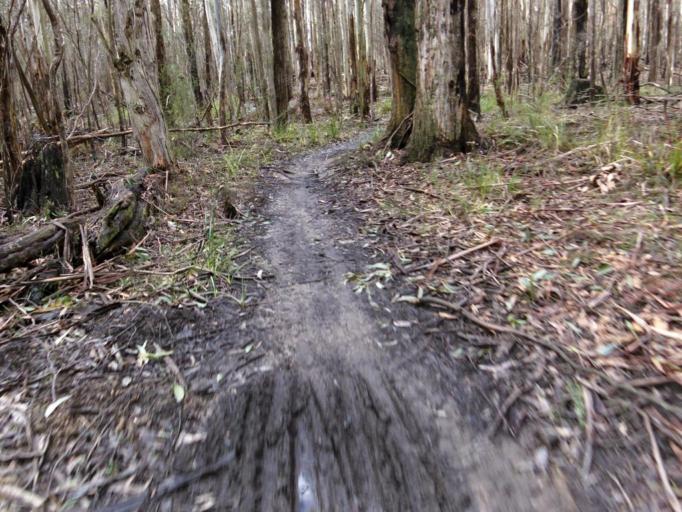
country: AU
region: Victoria
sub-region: Moorabool
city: Bacchus Marsh
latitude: -37.4233
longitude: 144.4812
